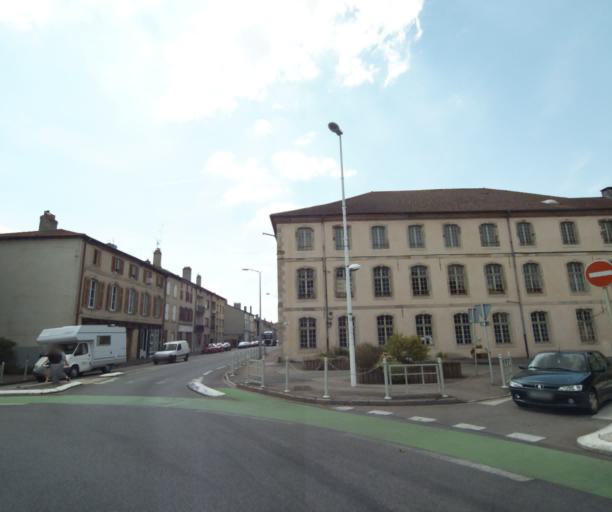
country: FR
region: Lorraine
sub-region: Departement de Meurthe-et-Moselle
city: Luneville
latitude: 48.5977
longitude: 6.4890
